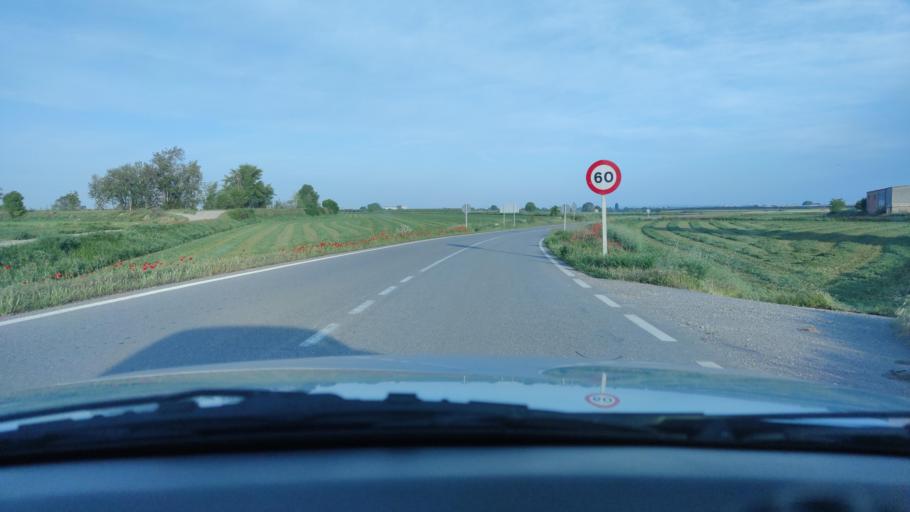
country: ES
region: Catalonia
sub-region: Provincia de Lleida
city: Ivars d'Urgell
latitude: 41.6719
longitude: 0.9889
